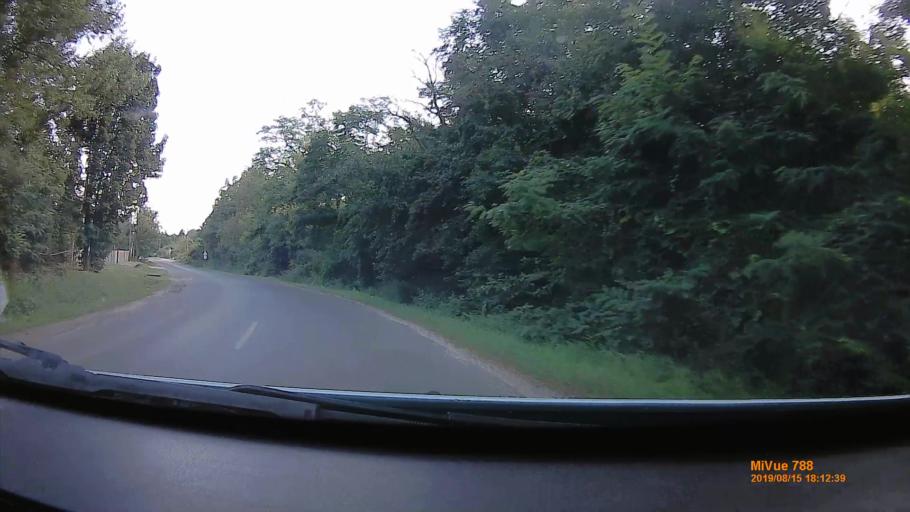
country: HU
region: Borsod-Abauj-Zemplen
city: Sajobabony
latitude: 48.1137
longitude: 20.7174
